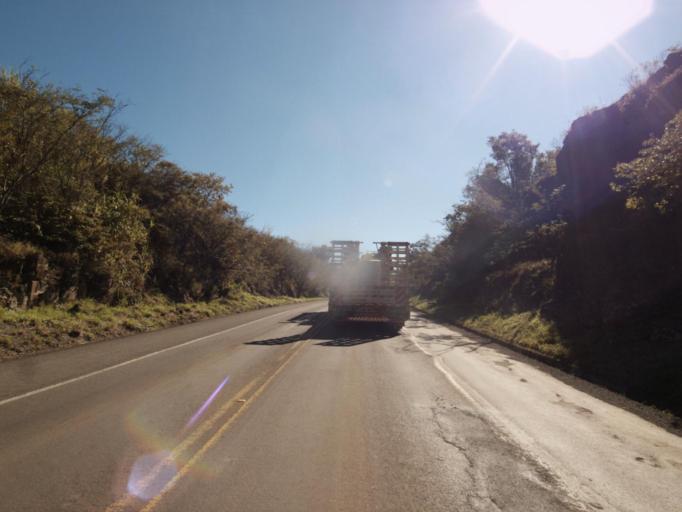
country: BR
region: Rio Grande do Sul
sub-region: Frederico Westphalen
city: Frederico Westphalen
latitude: -26.8124
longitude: -53.4367
